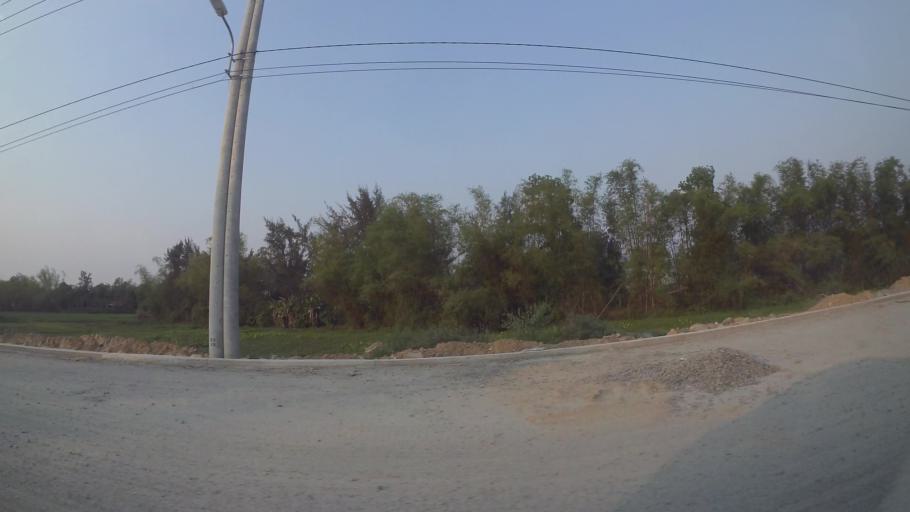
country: VN
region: Da Nang
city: Ngu Hanh Son
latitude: 15.9554
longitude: 108.2386
